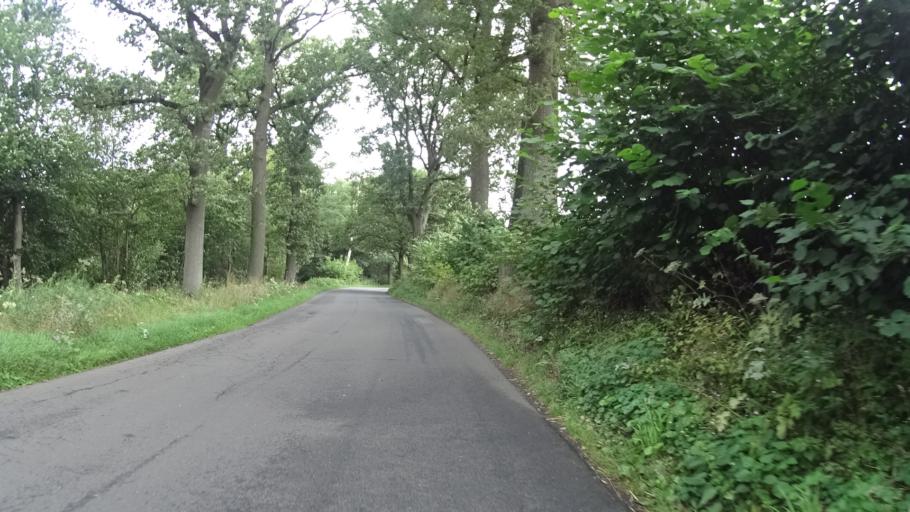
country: DE
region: Hamburg
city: Duvenstedt
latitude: 53.7210
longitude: 10.1204
